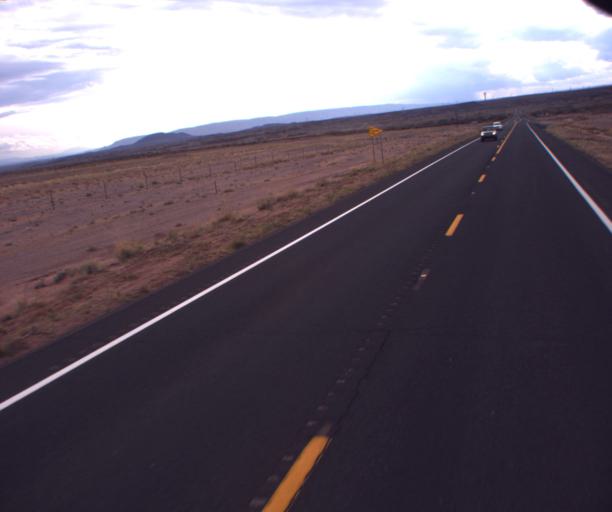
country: US
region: Arizona
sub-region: Coconino County
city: Tuba City
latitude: 36.0809
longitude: -111.3728
